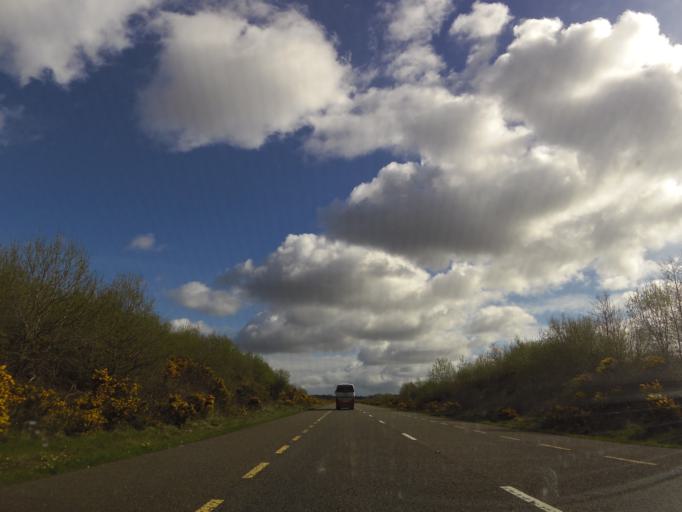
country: IE
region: Connaught
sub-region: Maigh Eo
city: Kiltamagh
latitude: 53.8033
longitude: -8.9143
